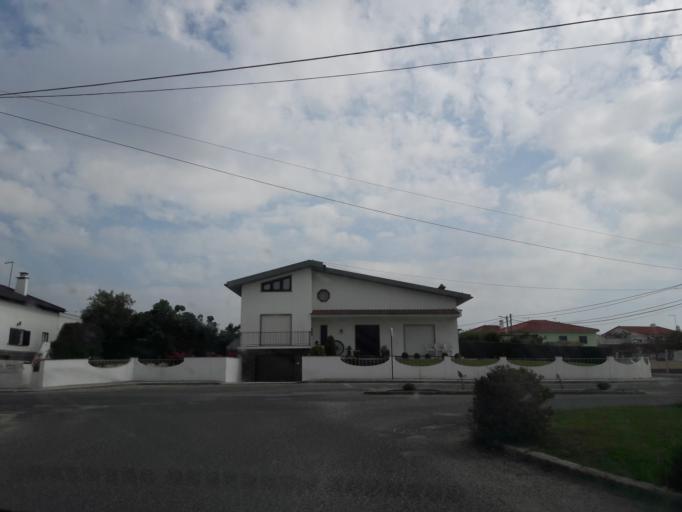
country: PT
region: Leiria
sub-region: Peniche
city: Atouguia da Baleia
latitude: 39.3382
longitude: -9.3285
